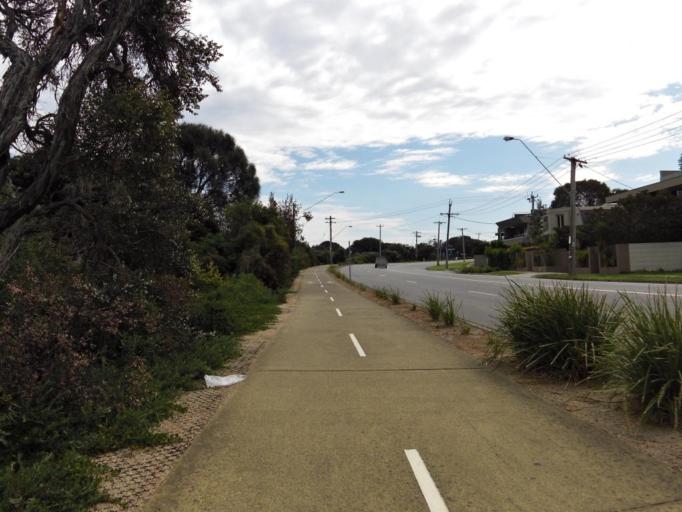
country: AU
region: Victoria
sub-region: Bayside
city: Black Rock
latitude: -37.9710
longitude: 145.0122
